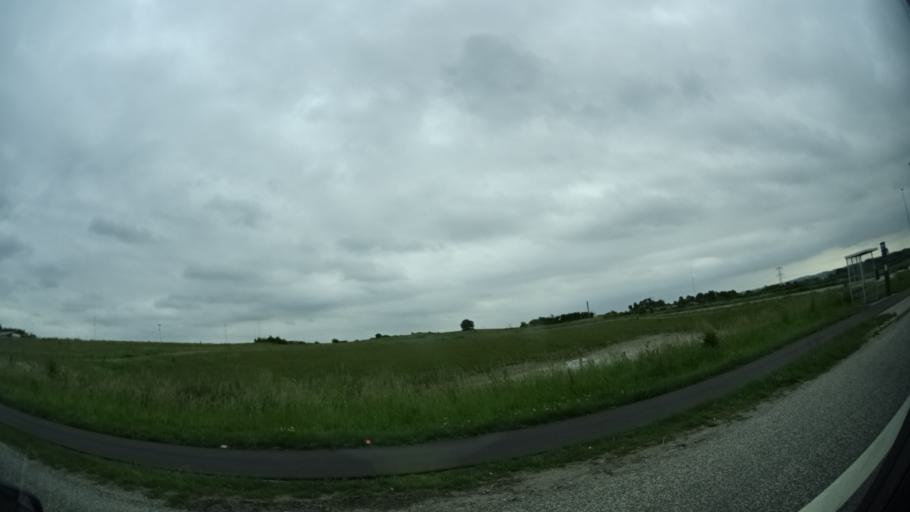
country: DK
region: Central Jutland
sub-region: Arhus Kommune
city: Kolt
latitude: 56.1006
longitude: 10.0625
